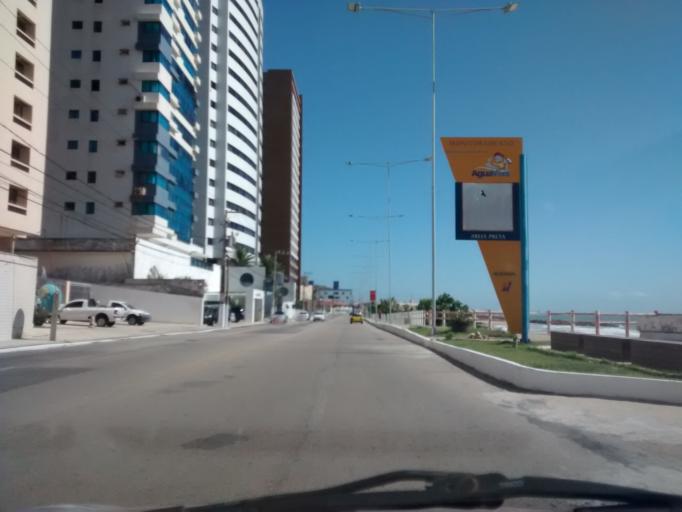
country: BR
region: Rio Grande do Norte
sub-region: Natal
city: Natal
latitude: -5.7892
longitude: -35.1887
